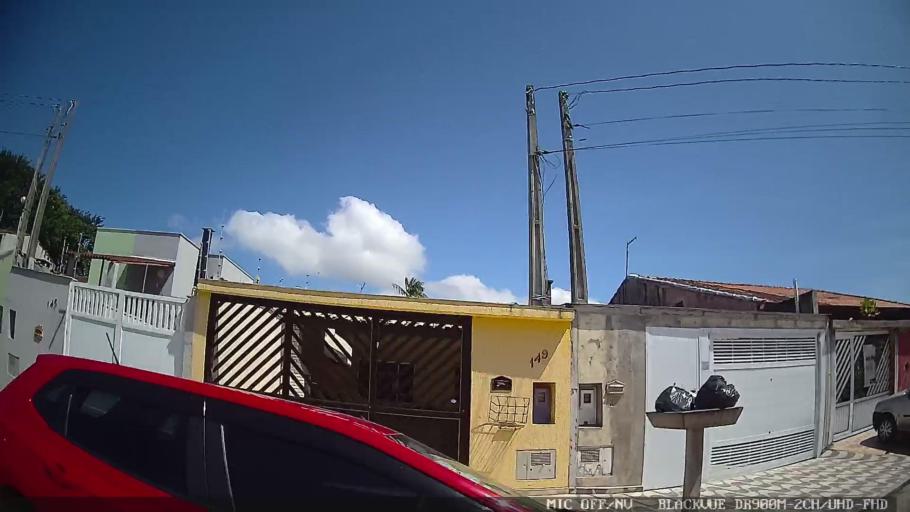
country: BR
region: Sao Paulo
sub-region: Peruibe
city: Peruibe
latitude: -24.3089
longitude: -46.9999
